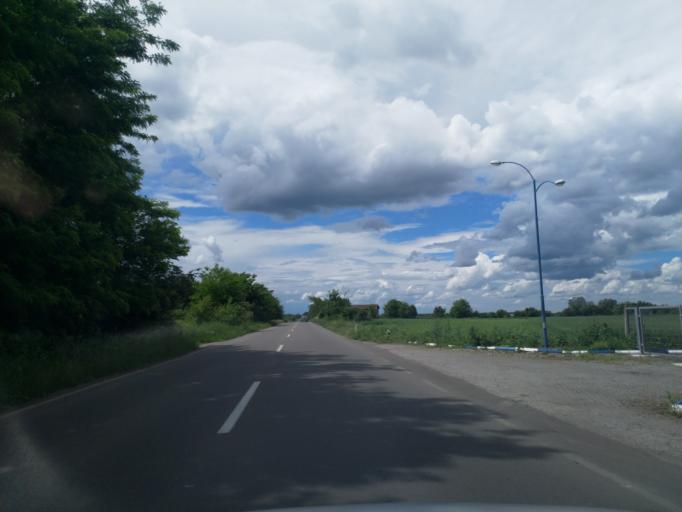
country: RS
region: Central Serbia
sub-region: Pomoravski Okrug
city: Paracin
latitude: 43.8788
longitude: 21.3917
